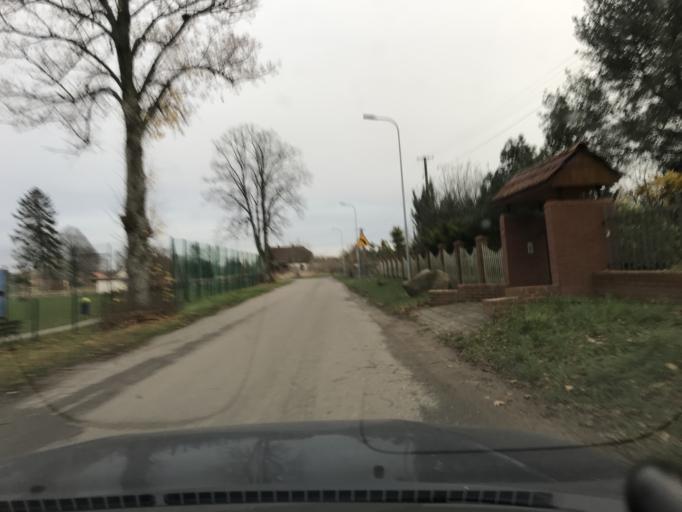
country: PL
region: Pomeranian Voivodeship
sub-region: Powiat slupski
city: Kobylnica
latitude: 54.4470
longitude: 16.8847
